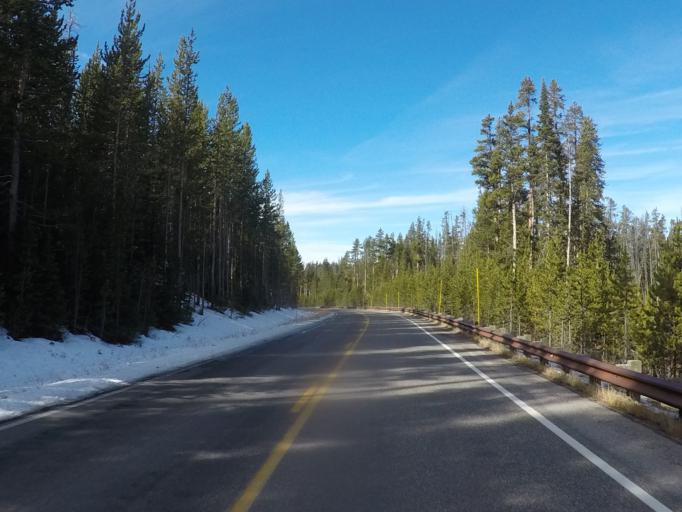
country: US
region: Montana
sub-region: Gallatin County
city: West Yellowstone
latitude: 44.4312
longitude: -110.7731
